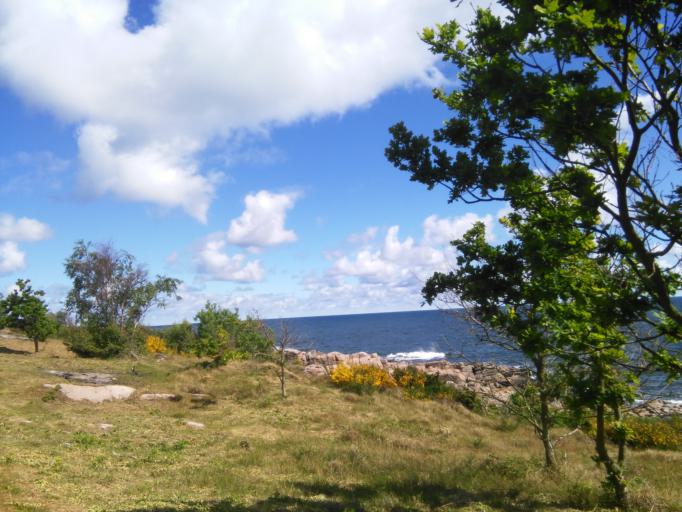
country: DK
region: Capital Region
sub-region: Bornholm Kommune
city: Ronne
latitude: 55.2951
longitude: 14.7777
